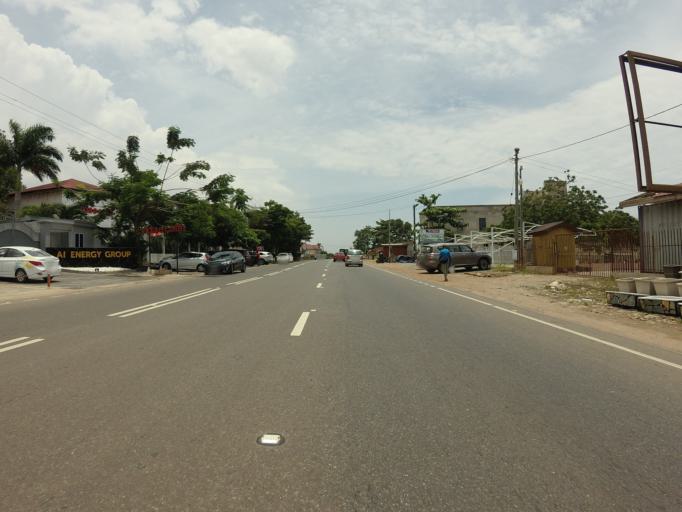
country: GH
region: Greater Accra
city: Medina Estates
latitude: 5.6342
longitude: -0.1477
